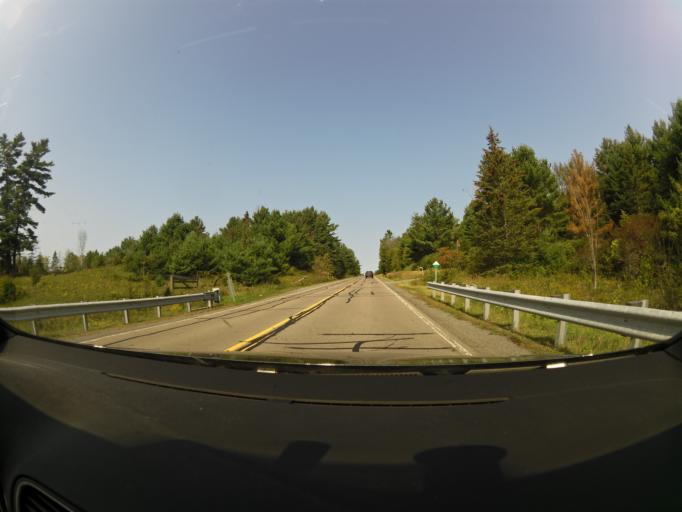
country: CA
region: Ontario
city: Arnprior
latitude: 45.4341
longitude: -76.1722
